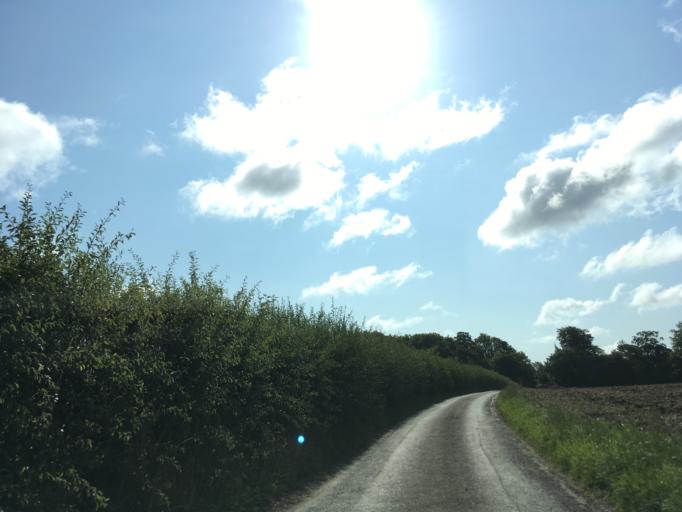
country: GB
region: England
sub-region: South Gloucestershire
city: Hinton
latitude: 51.5068
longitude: -2.3537
